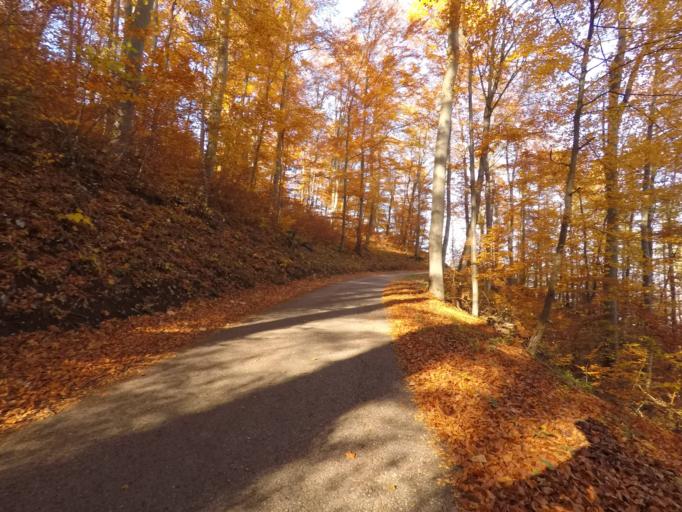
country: DE
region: Baden-Wuerttemberg
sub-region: Tuebingen Region
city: Pfullingen
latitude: 48.4427
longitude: 9.2313
